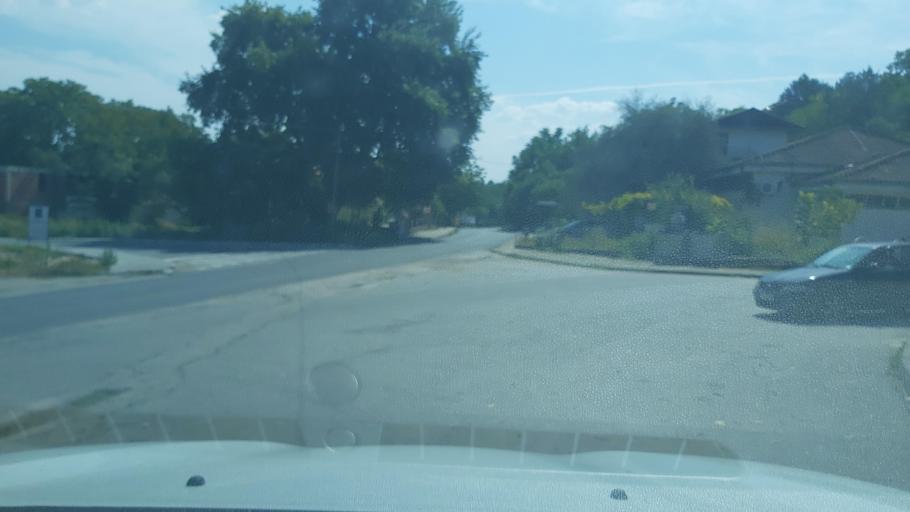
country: MK
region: Dojran
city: Star Dojran
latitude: 41.1792
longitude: 22.7243
